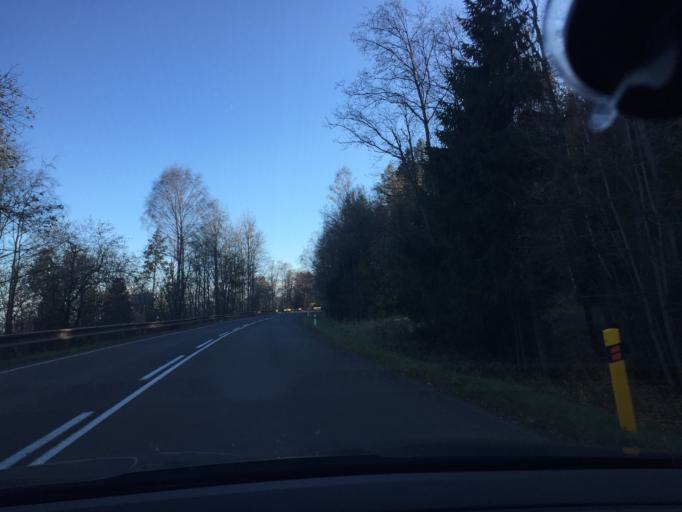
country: SK
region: Presovsky
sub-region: Okres Poprad
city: Vysoke Tatry
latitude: 49.1603
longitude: 20.2724
